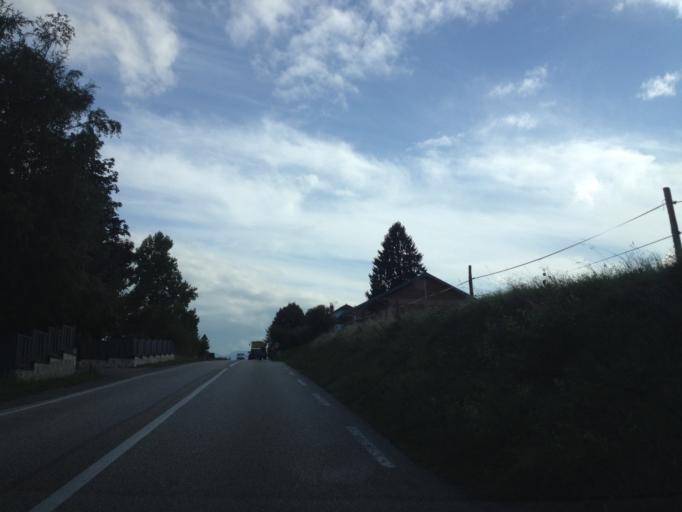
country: FR
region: Rhone-Alpes
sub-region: Departement de la Savoie
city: Le Bourget-du-Lac
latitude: 45.6371
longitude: 5.8628
